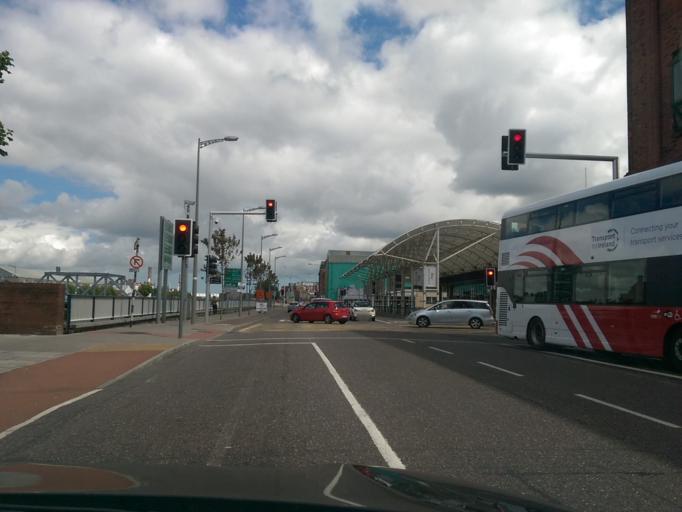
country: IE
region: Munster
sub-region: County Cork
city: Cork
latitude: 51.9000
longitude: -8.4677
